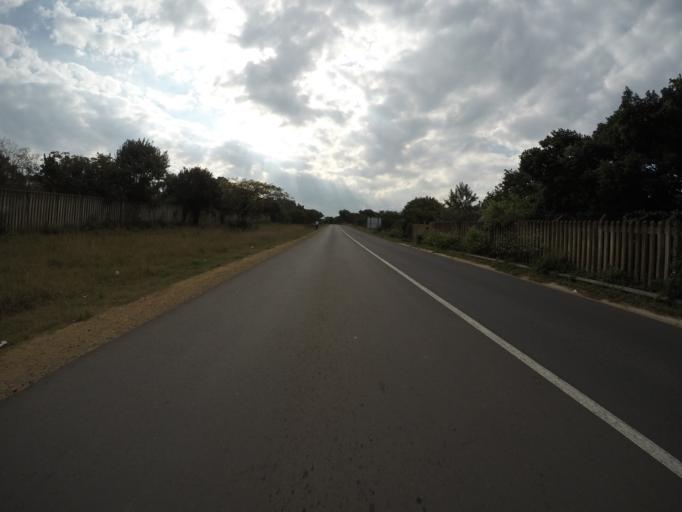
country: ZA
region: KwaZulu-Natal
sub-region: uThungulu District Municipality
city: Richards Bay
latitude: -28.7473
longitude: 32.0853
